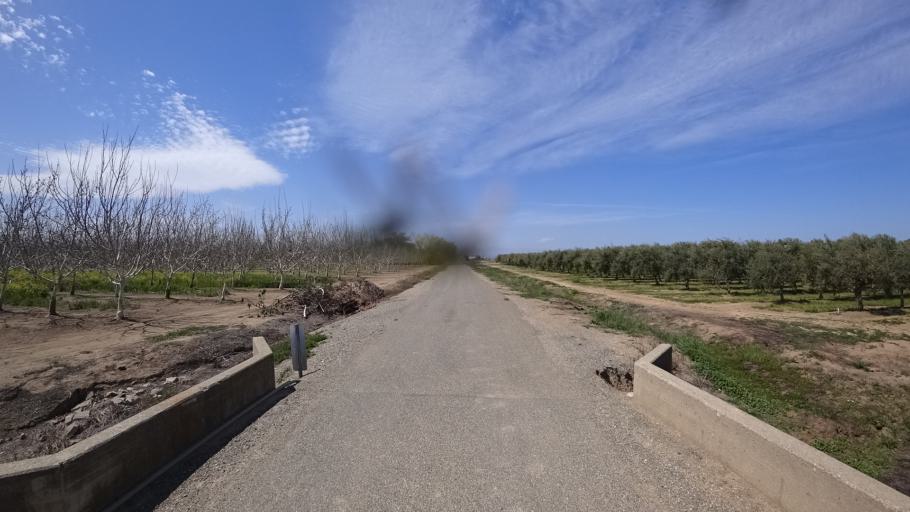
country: US
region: California
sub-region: Glenn County
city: Willows
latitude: 39.5769
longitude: -122.1961
